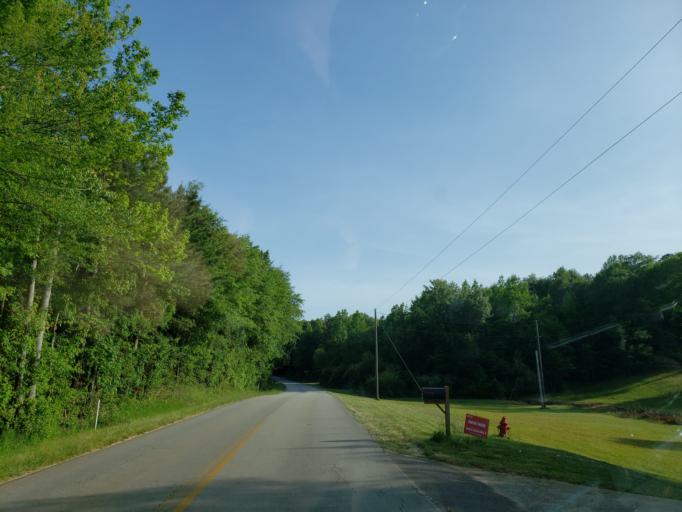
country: US
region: Georgia
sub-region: Carroll County
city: Bowdon
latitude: 33.4809
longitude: -85.3019
